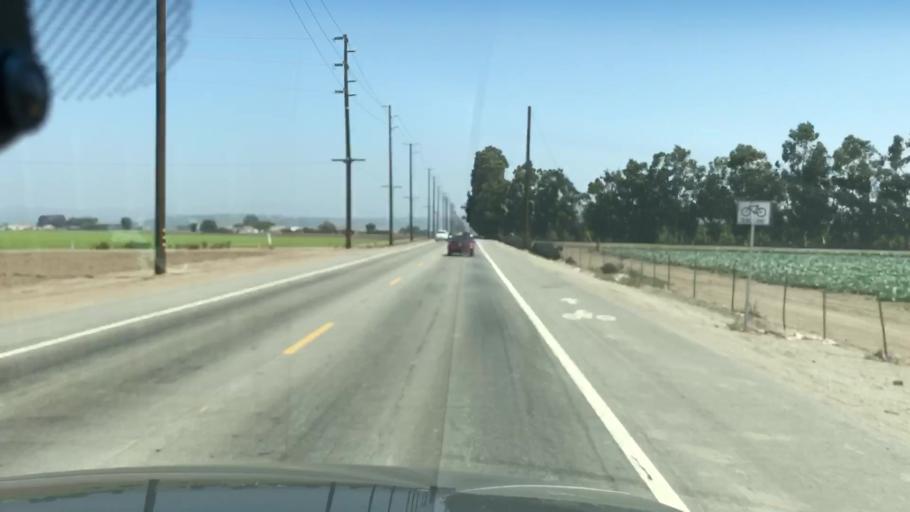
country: US
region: California
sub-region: Ventura County
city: Oxnard
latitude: 34.1816
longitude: -119.1185
